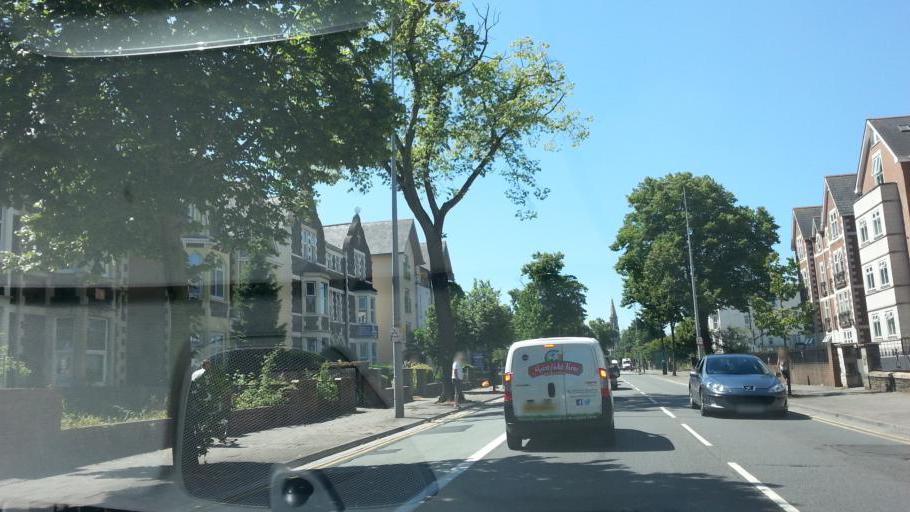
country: GB
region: Wales
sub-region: Cardiff
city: Cardiff
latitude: 51.4898
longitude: -3.1574
